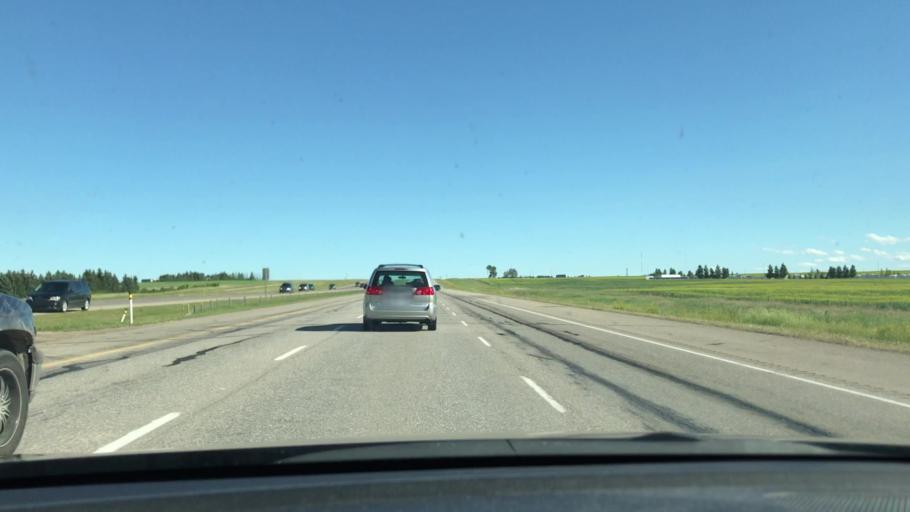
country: CA
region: Alberta
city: Crossfield
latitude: 51.4531
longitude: -114.0174
